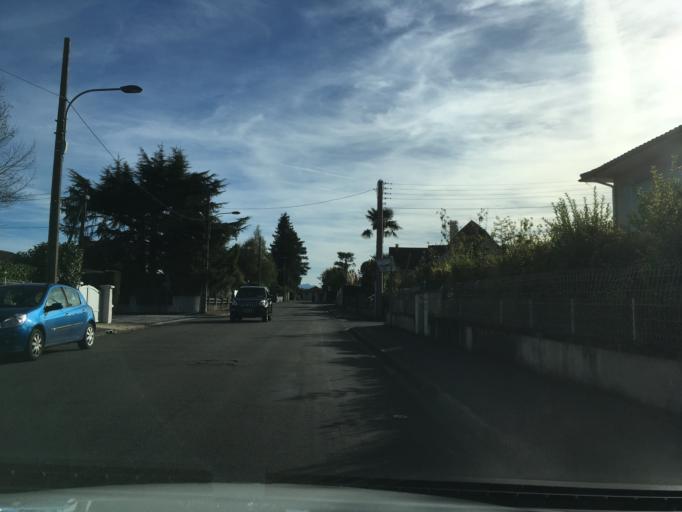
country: FR
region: Aquitaine
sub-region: Departement des Pyrenees-Atlantiques
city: Pau
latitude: 43.3262
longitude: -0.3741
